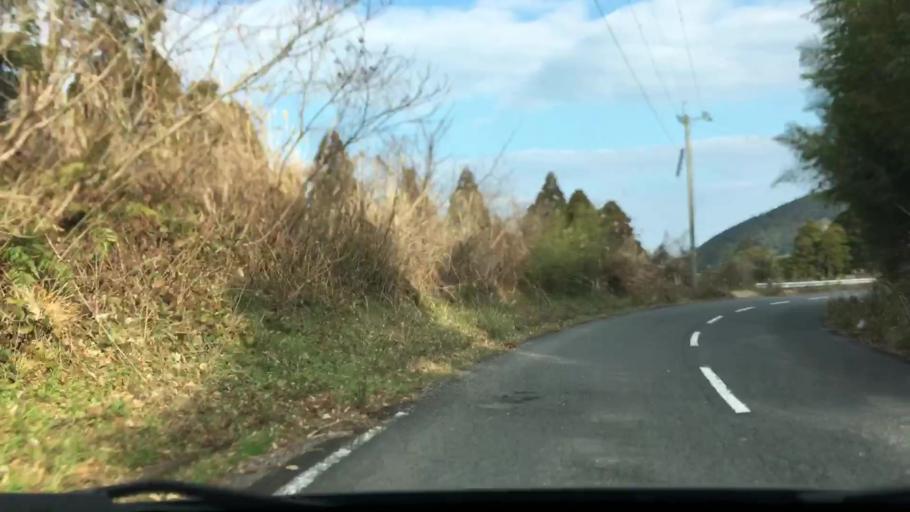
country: JP
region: Miyazaki
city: Nichinan
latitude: 31.6102
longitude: 131.3306
